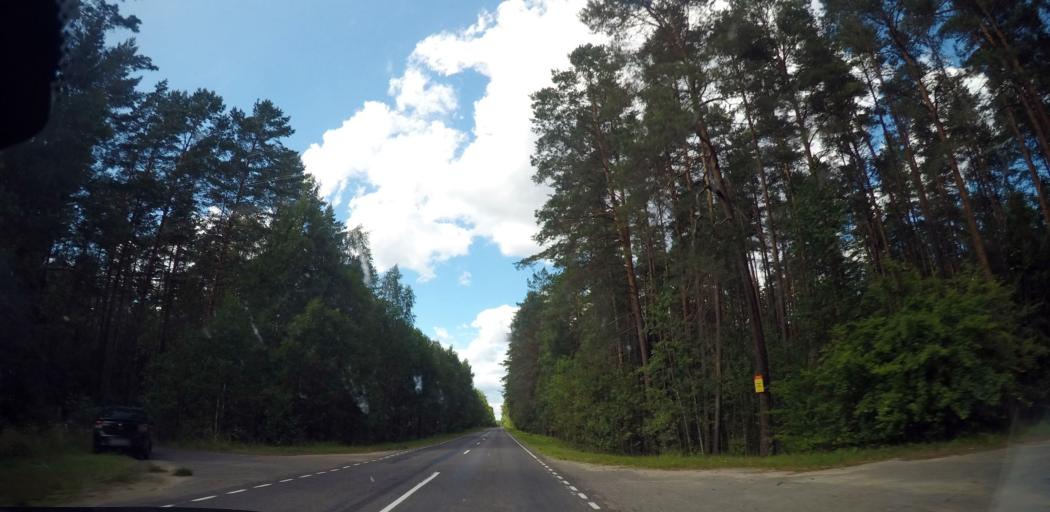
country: BY
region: Grodnenskaya
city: Skidal'
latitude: 53.8432
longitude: 24.2105
